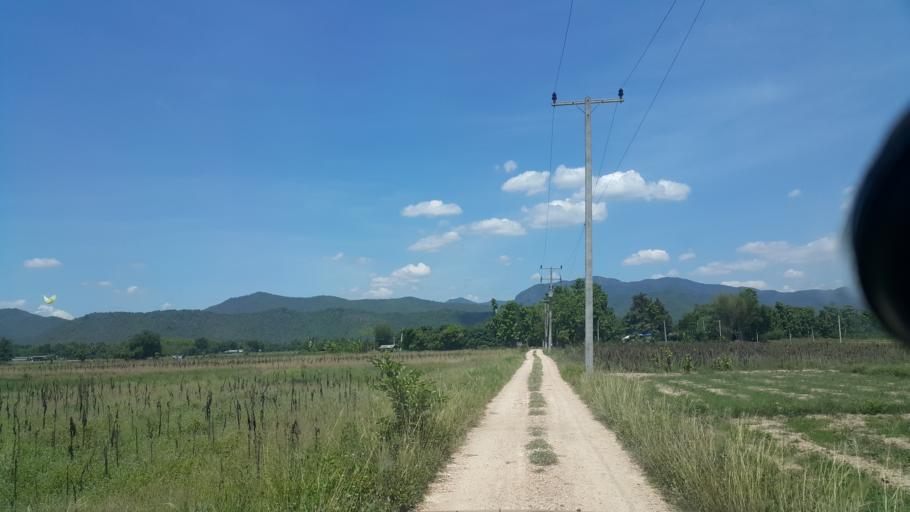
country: TH
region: Chiang Mai
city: San Kamphaeng
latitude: 18.7009
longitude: 99.1496
